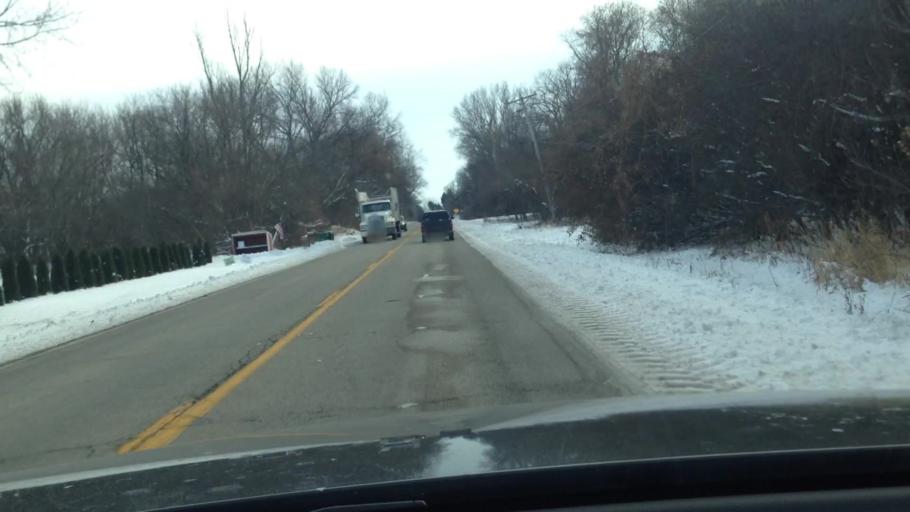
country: US
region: Illinois
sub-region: McHenry County
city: Hebron
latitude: 42.4855
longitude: -88.4426
